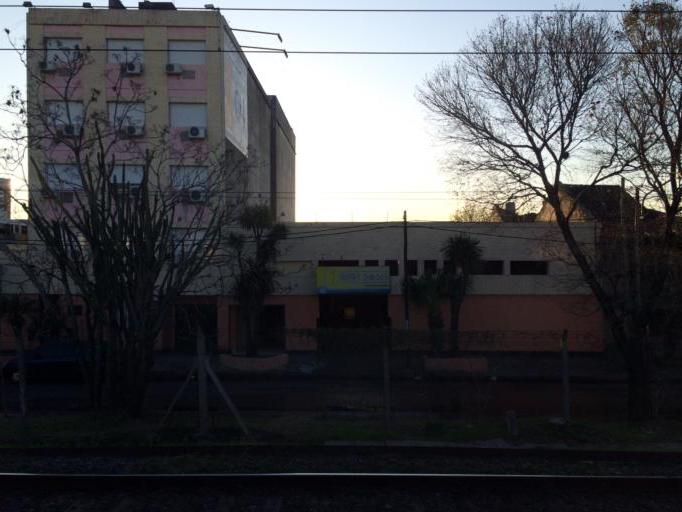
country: AR
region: Buenos Aires
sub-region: Partido de Lanus
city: Lanus
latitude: -34.6994
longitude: -58.3876
